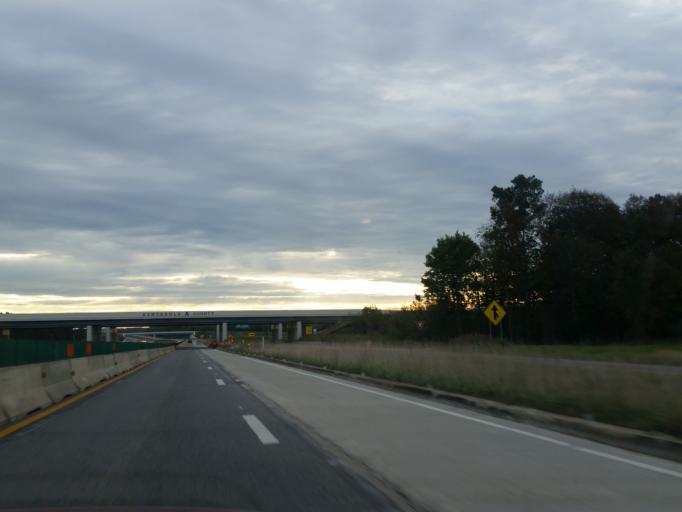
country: US
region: Ohio
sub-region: Ashtabula County
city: Ashtabula
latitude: 41.8278
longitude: -80.7674
